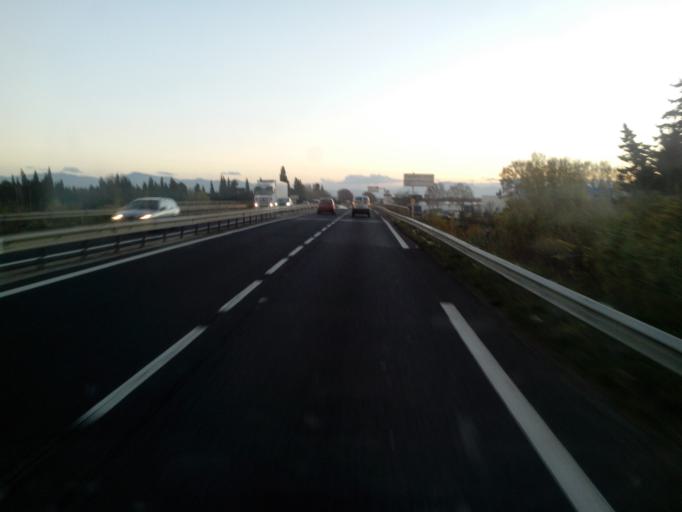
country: FR
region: Languedoc-Roussillon
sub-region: Departement des Pyrenees-Orientales
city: Rivesaltes
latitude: 42.7735
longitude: 2.9015
